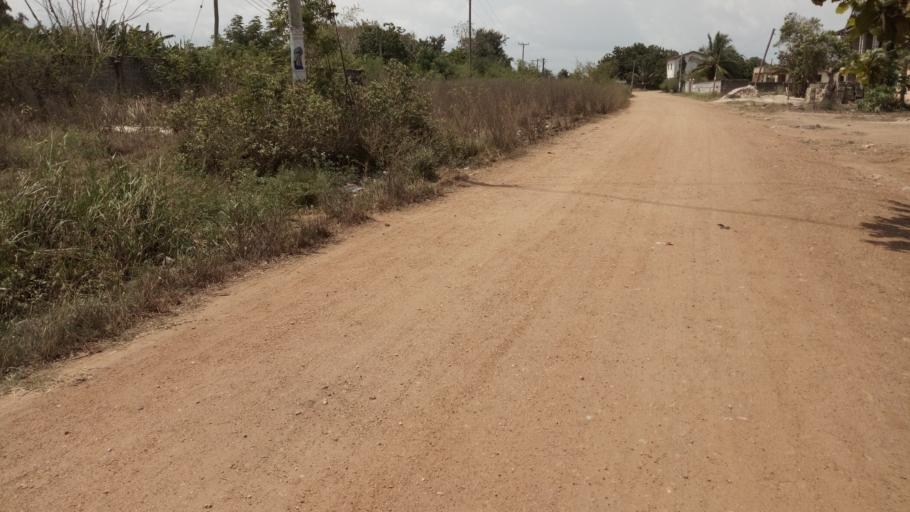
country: GH
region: Central
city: Winneba
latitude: 5.3547
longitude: -0.6357
